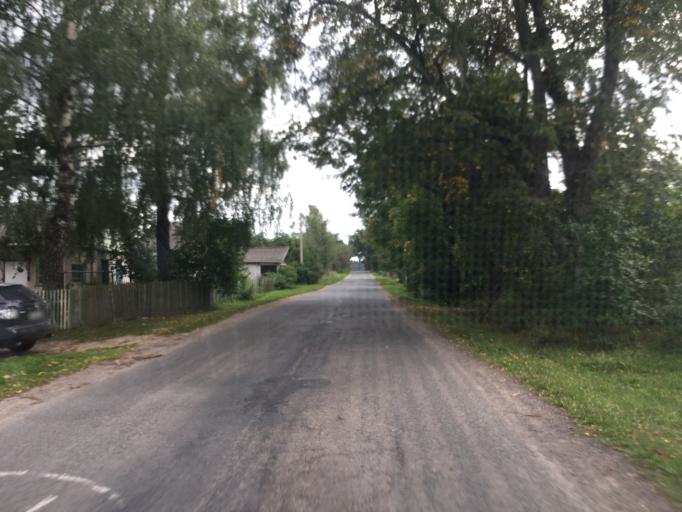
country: BY
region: Vitebsk
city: Vitebsk
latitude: 55.1452
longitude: 30.2839
